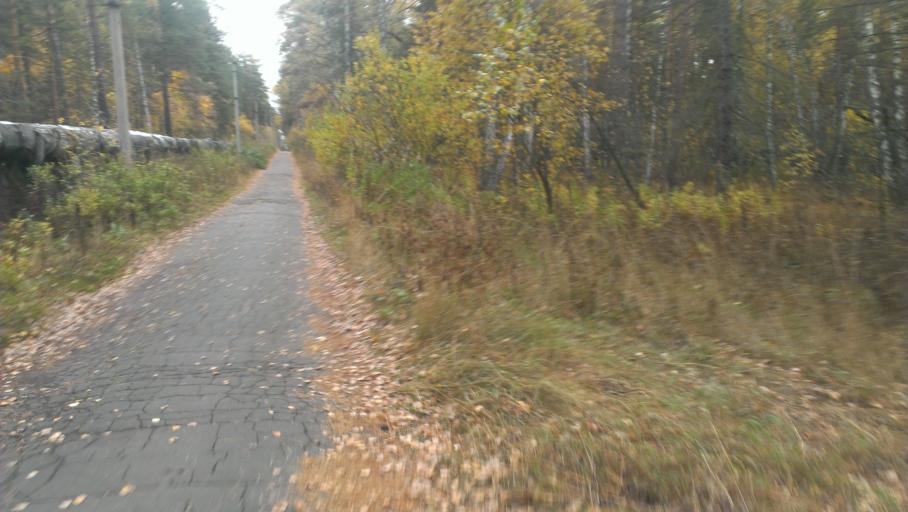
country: RU
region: Altai Krai
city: Yuzhnyy
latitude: 53.2639
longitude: 83.6857
